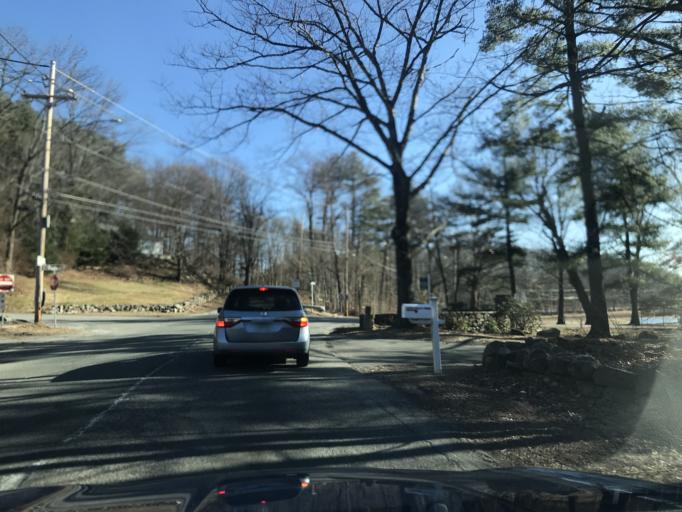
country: US
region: Massachusetts
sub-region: Essex County
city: North Andover
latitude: 42.7131
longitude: -71.0890
